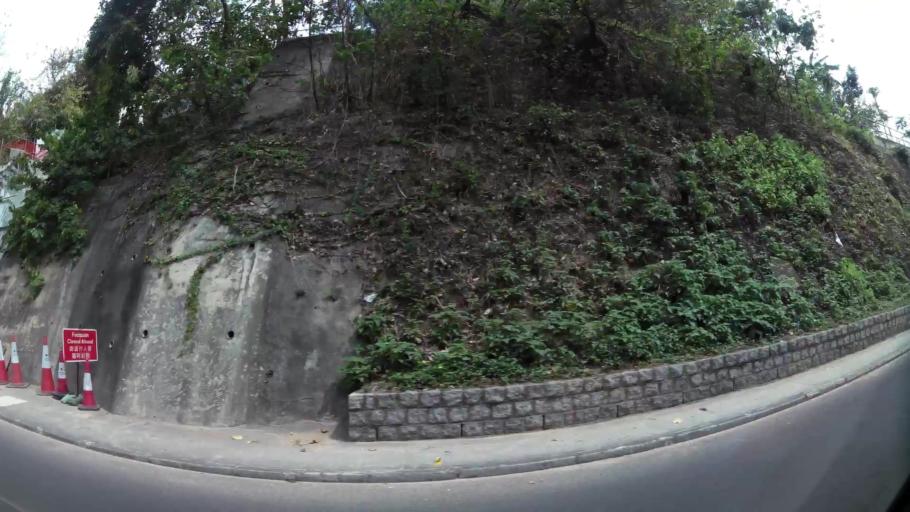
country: HK
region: Sham Shui Po
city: Sham Shui Po
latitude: 22.3378
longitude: 114.1626
